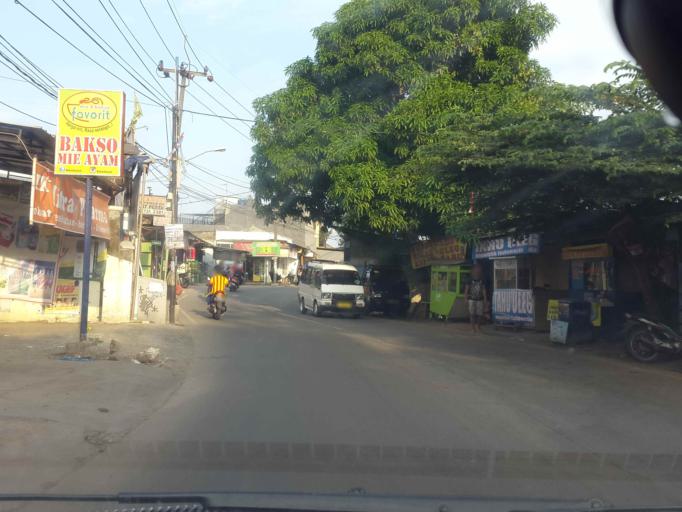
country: ID
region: Banten
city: South Tangerang
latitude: -6.2632
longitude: 106.7127
